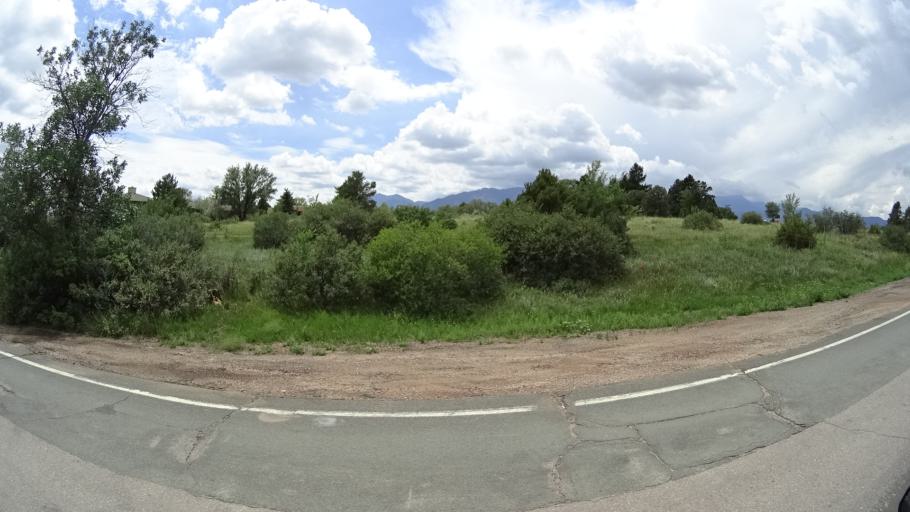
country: US
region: Colorado
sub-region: El Paso County
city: Colorado Springs
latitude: 38.8542
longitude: -104.8432
